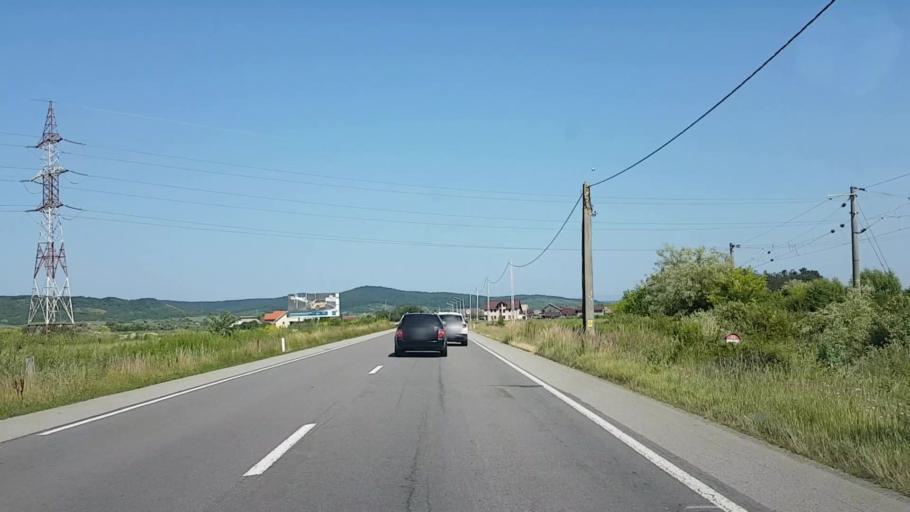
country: RO
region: Bistrita-Nasaud
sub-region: Comuna Sintereag
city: Cociu
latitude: 47.1812
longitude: 24.2615
